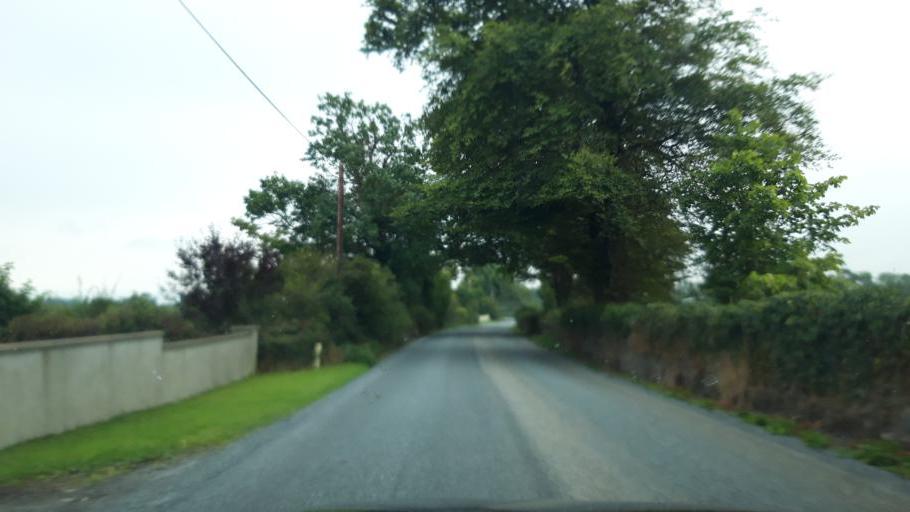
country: IE
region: Munster
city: Fethard
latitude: 52.4309
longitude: -7.6994
